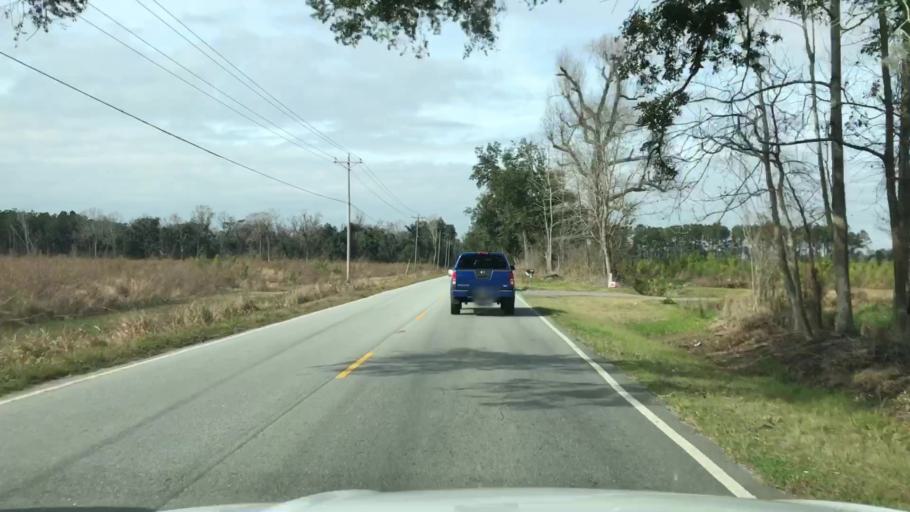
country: US
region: South Carolina
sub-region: Charleston County
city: Shell Point
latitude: 32.7726
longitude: -80.0822
